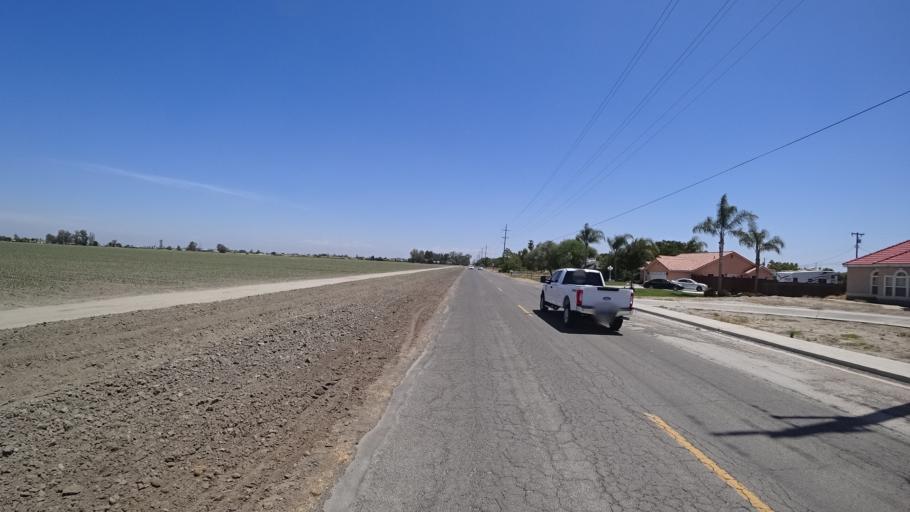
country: US
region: California
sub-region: Kings County
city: Corcoran
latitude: 36.1091
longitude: -119.5839
